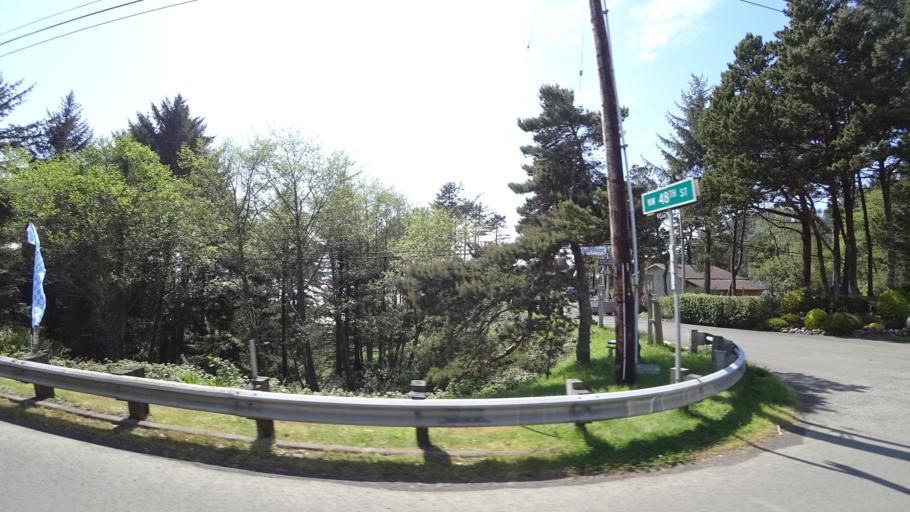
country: US
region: Oregon
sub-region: Lincoln County
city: Newport
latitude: 44.6723
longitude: -124.0591
